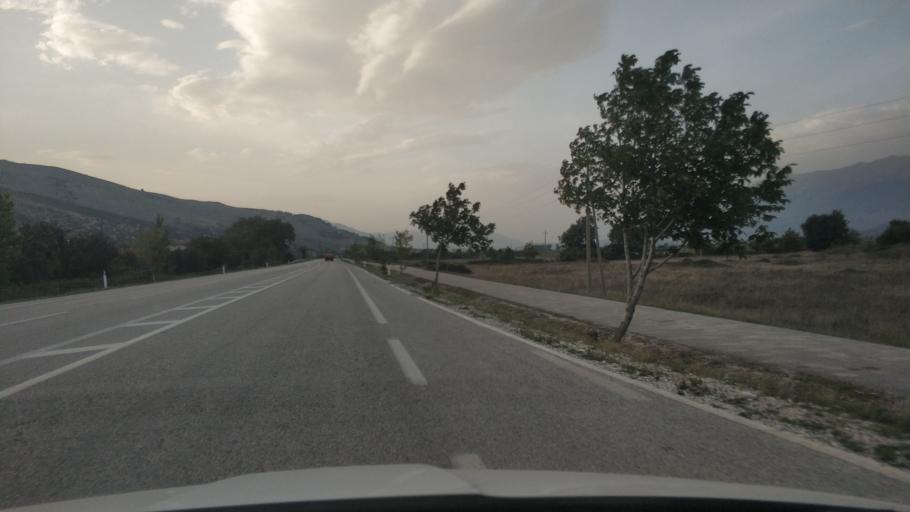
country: AL
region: Gjirokaster
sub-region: Rrethi i Gjirokastres
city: Libohove
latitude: 39.9528
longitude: 20.2535
